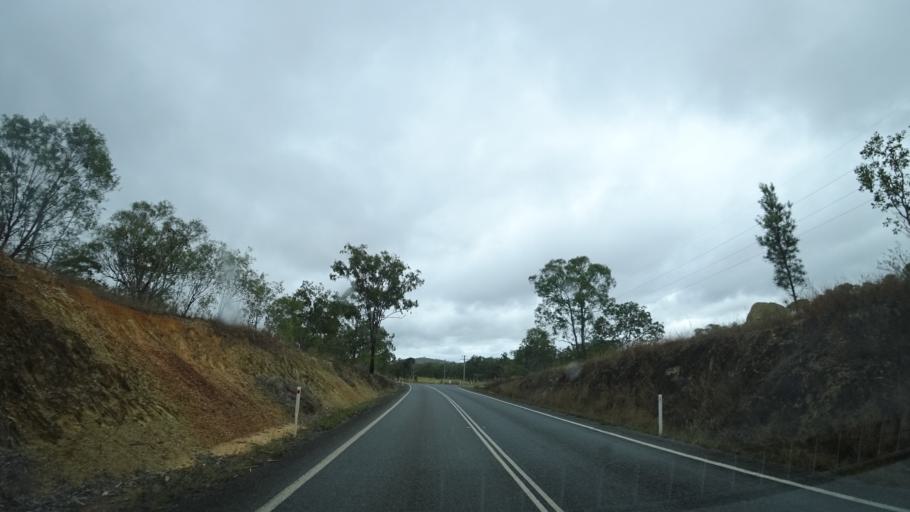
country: AU
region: Queensland
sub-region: Cairns
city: Port Douglas
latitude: -16.6834
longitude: 145.3314
